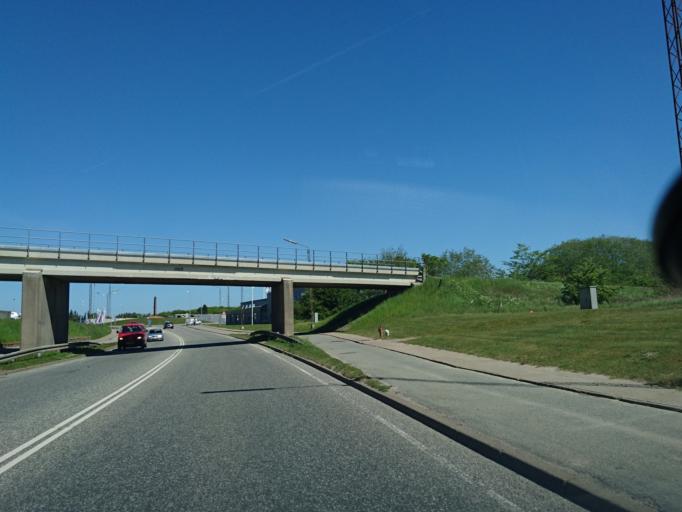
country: DK
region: North Denmark
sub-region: Hjorring Kommune
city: Hjorring
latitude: 57.4541
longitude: 10.0172
